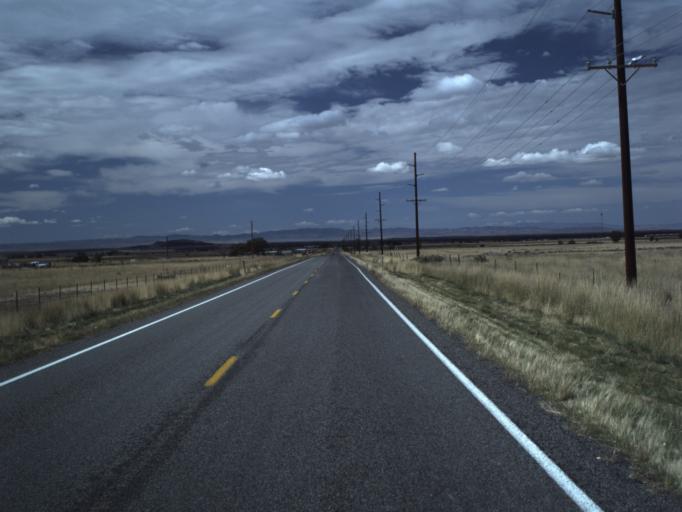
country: US
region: Utah
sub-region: Millard County
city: Fillmore
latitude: 38.9792
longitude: -112.3872
